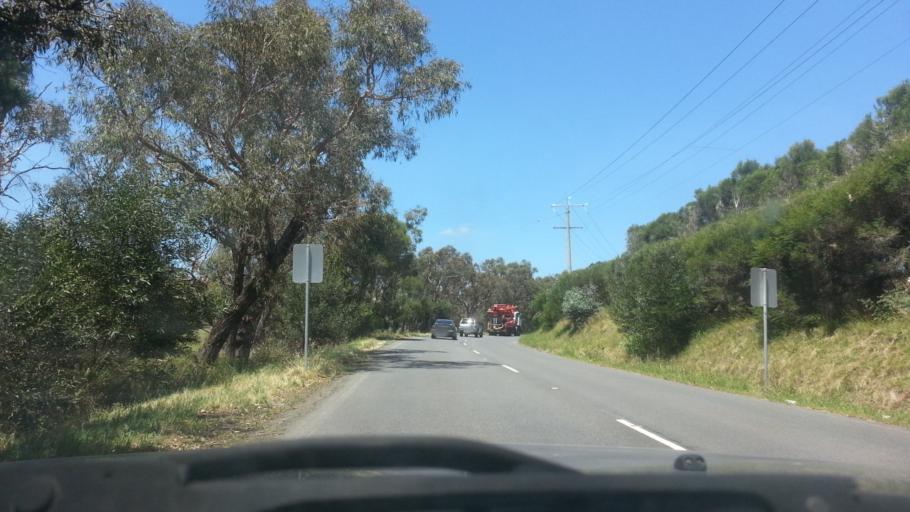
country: AU
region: Victoria
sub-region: Cardinia
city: Beaconsfield Upper
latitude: -37.9798
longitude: 145.3933
